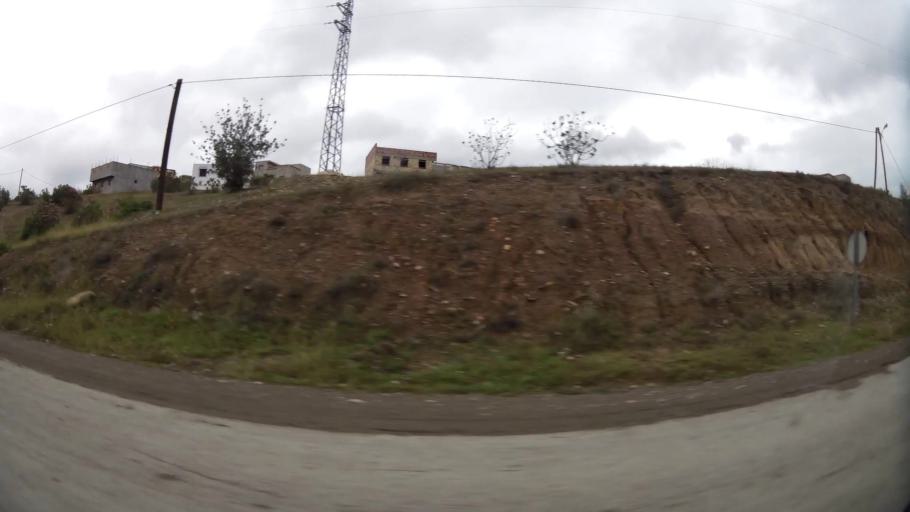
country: MA
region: Taza-Al Hoceima-Taounate
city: Imzourene
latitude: 34.9603
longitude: -3.8113
